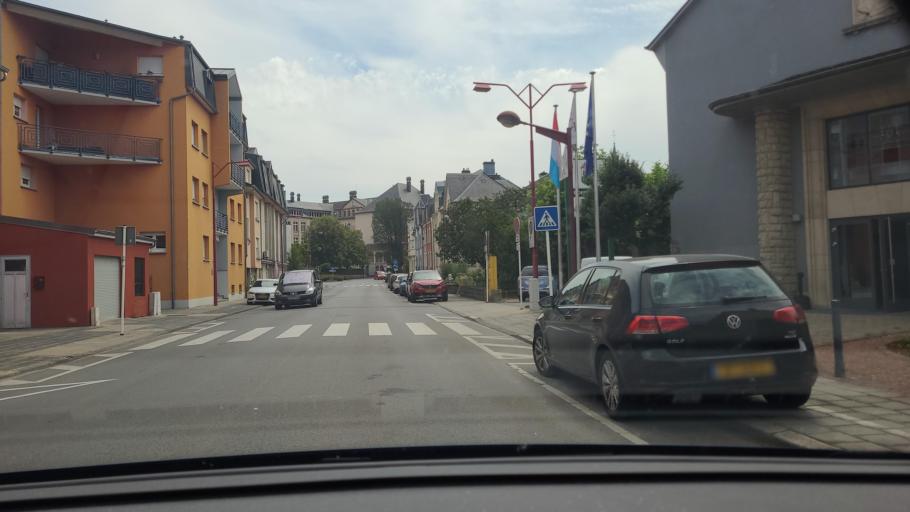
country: LU
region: Luxembourg
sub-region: Canton d'Esch-sur-Alzette
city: Petange
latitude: 49.5594
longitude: 5.8735
